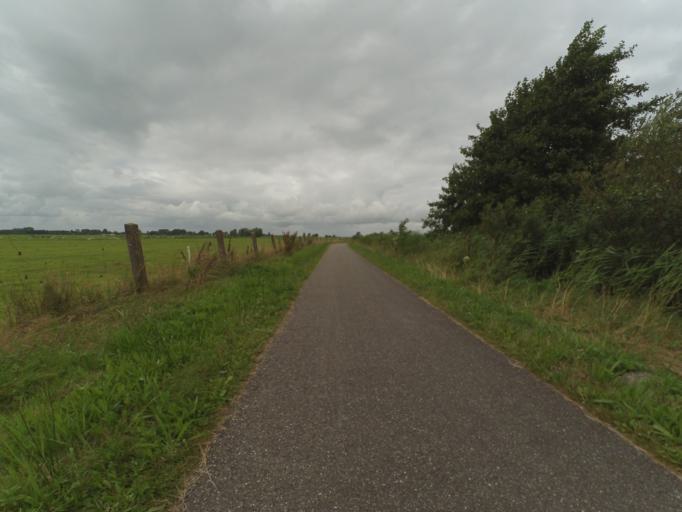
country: NL
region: Friesland
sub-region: Gemeente Kollumerland en Nieuwkruisland
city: Kollumerzwaag
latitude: 53.2891
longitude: 6.1087
